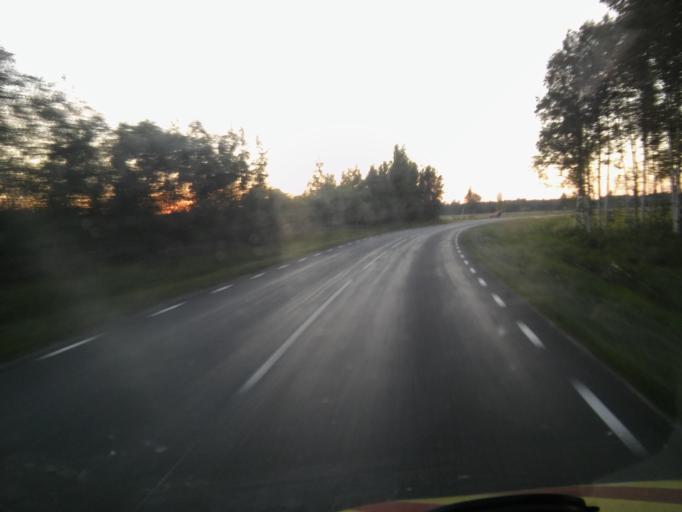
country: EE
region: Paernumaa
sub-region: Paikuse vald
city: Paikuse
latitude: 58.2990
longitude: 24.6862
